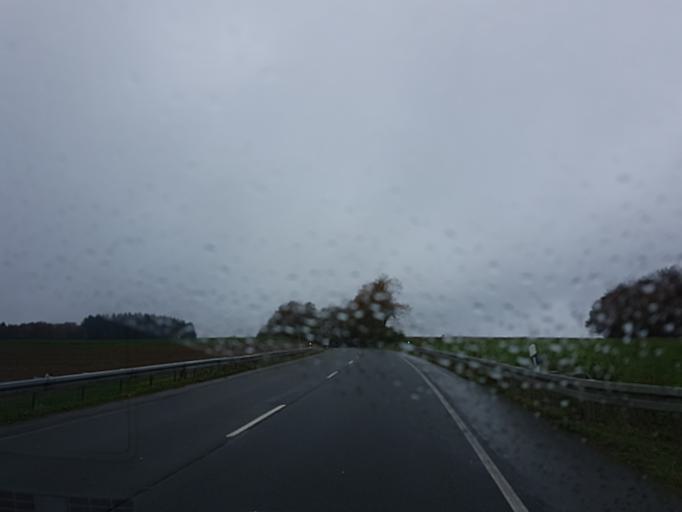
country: DE
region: North Rhine-Westphalia
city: Meinerzhagen
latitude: 51.1029
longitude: 7.6169
